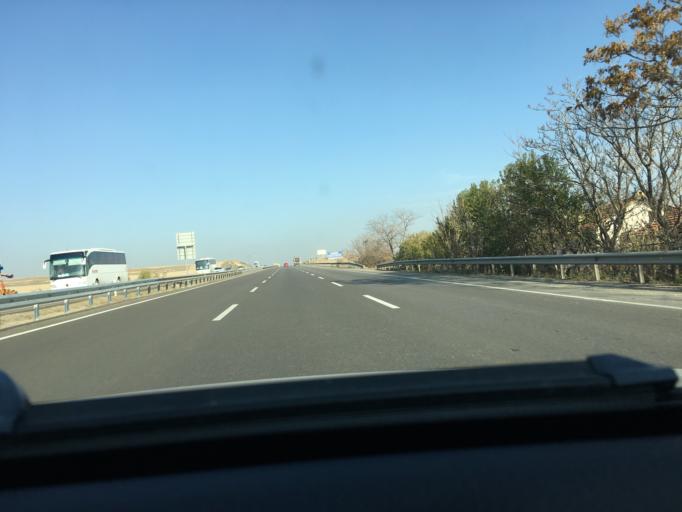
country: TR
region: Ankara
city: Temelli
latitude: 39.7365
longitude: 32.3912
